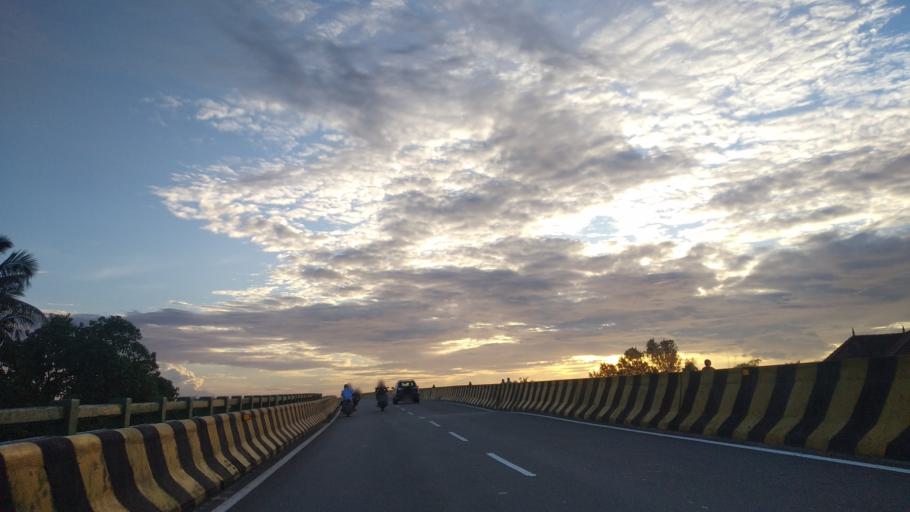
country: IN
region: Kerala
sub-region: Ernakulam
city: Elur
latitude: 10.0476
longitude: 76.2686
